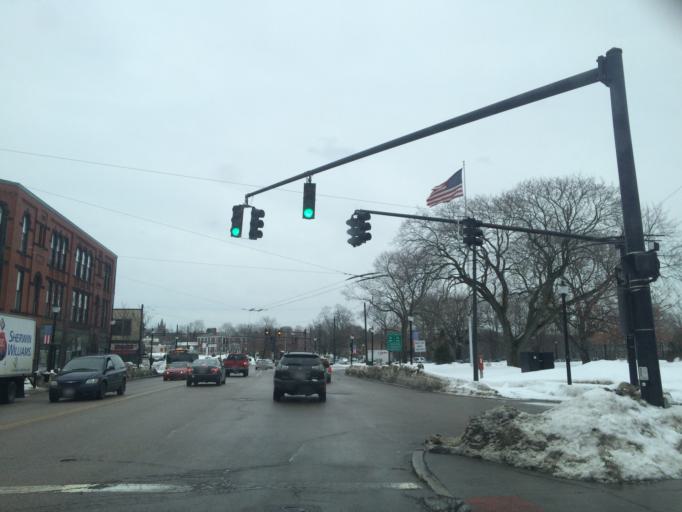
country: US
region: Massachusetts
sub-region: Middlesex County
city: Watertown
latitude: 42.3660
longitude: -71.1856
